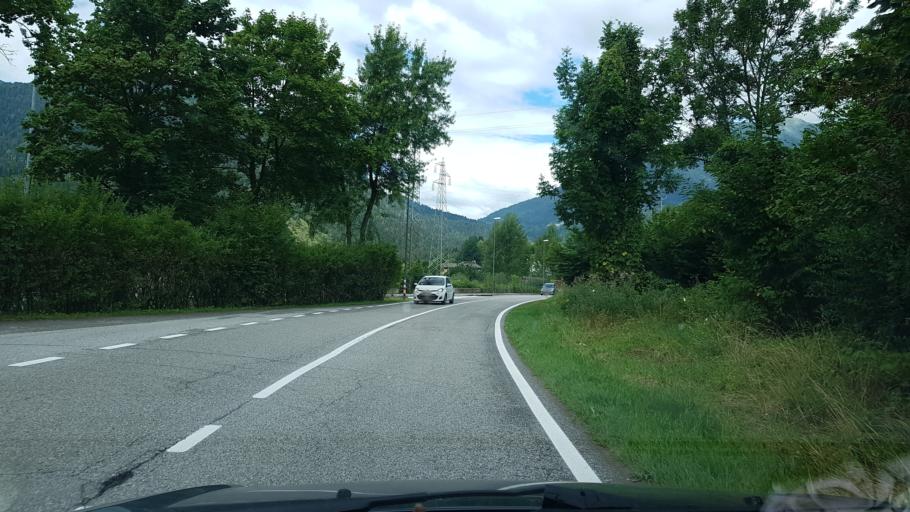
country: IT
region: Friuli Venezia Giulia
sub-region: Provincia di Udine
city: Cercivento
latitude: 46.5249
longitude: 13.0027
